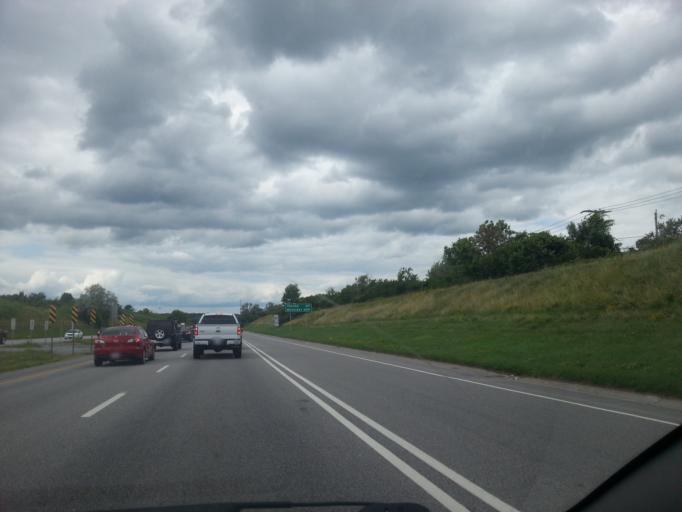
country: CA
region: Quebec
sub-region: Outaouais
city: Gatineau
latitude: 45.4771
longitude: -75.7136
